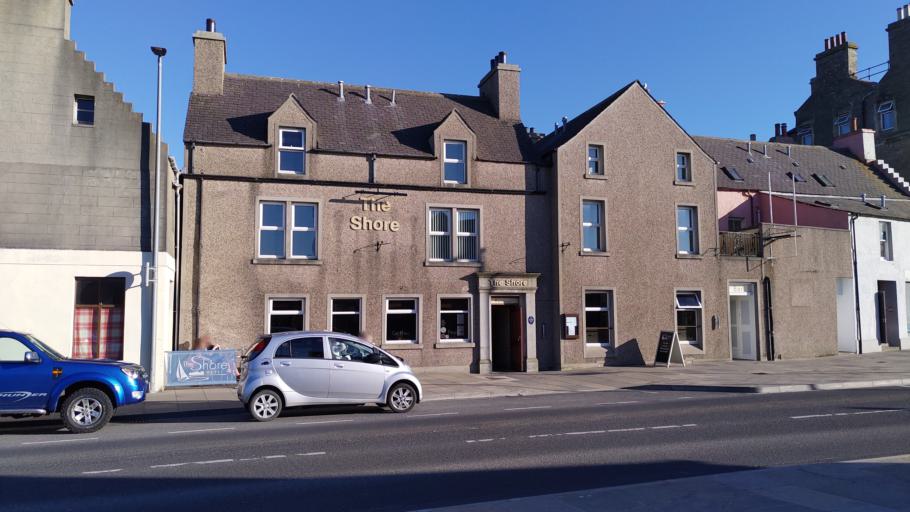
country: GB
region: Scotland
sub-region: Orkney Islands
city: Kirkwall
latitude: 58.9849
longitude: -2.9582
